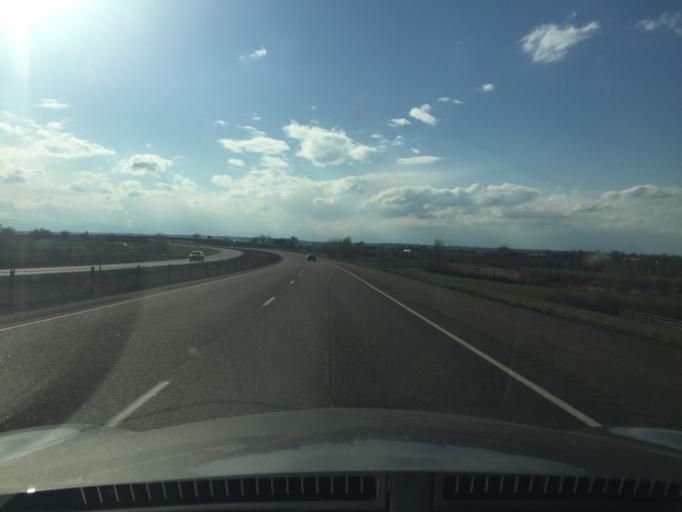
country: US
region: Colorado
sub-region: Adams County
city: Brighton
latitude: 39.9268
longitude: -104.8084
